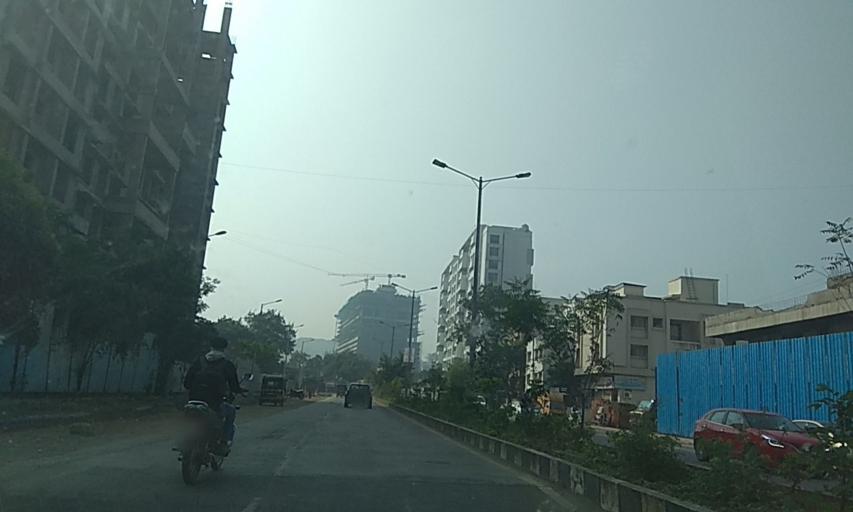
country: IN
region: Maharashtra
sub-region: Pune Division
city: Pimpri
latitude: 18.5612
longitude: 73.7767
